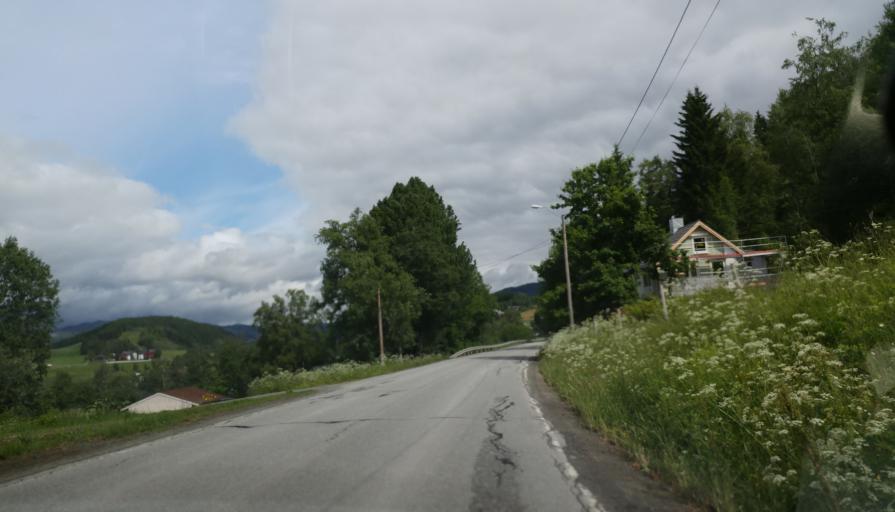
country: NO
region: Sor-Trondelag
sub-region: Selbu
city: Mebonden
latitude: 63.2357
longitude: 11.0404
